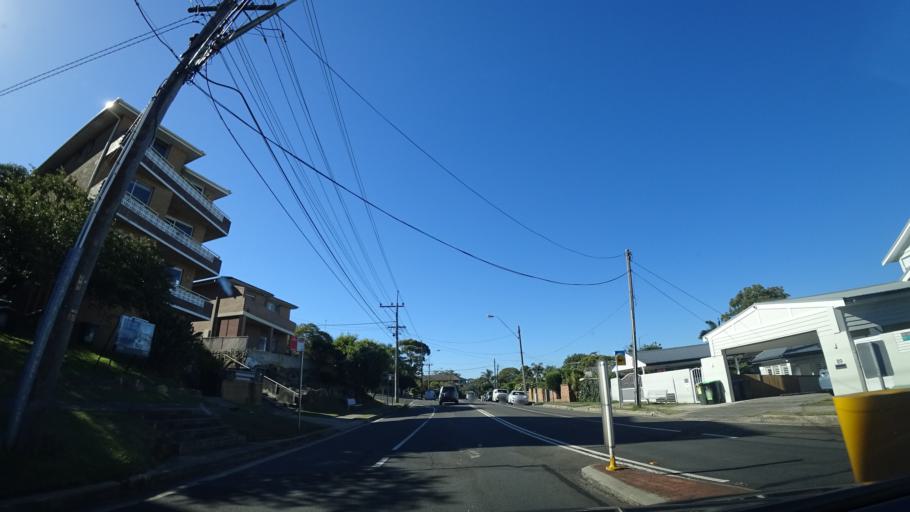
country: AU
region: New South Wales
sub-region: Warringah
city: Freshwater
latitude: -33.7757
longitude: 151.2794
